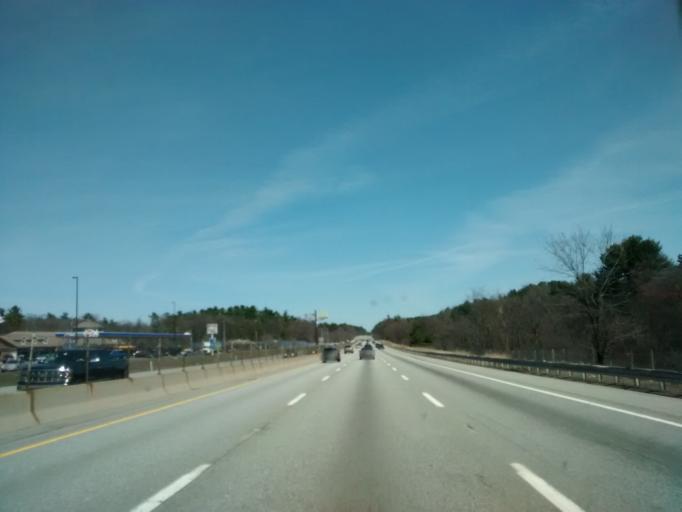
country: US
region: Massachusetts
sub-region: Middlesex County
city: Framingham Center
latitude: 42.3108
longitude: -71.4307
